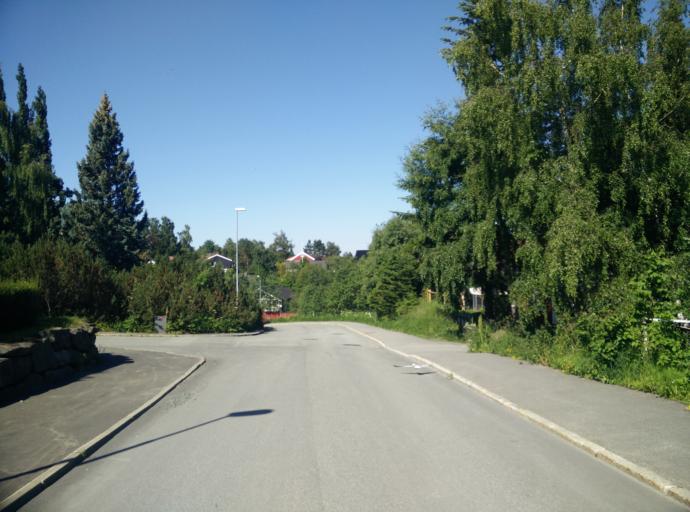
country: NO
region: Sor-Trondelag
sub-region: Trondheim
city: Trondheim
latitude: 63.4120
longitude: 10.3729
